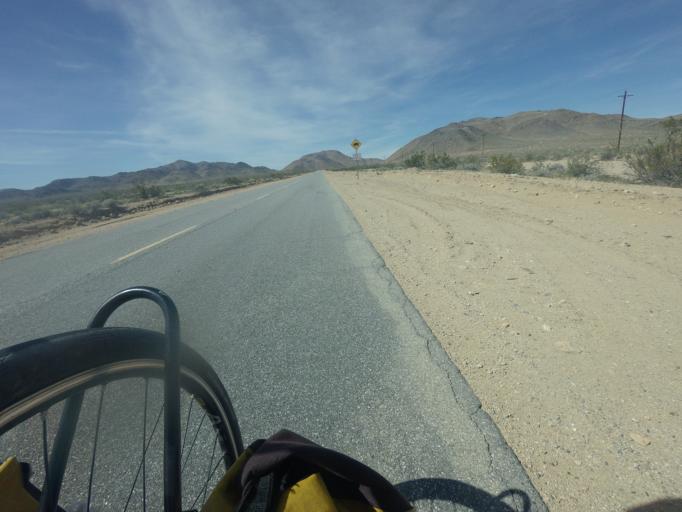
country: US
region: California
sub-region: San Bernardino County
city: Searles Valley
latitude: 35.5728
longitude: -117.4474
